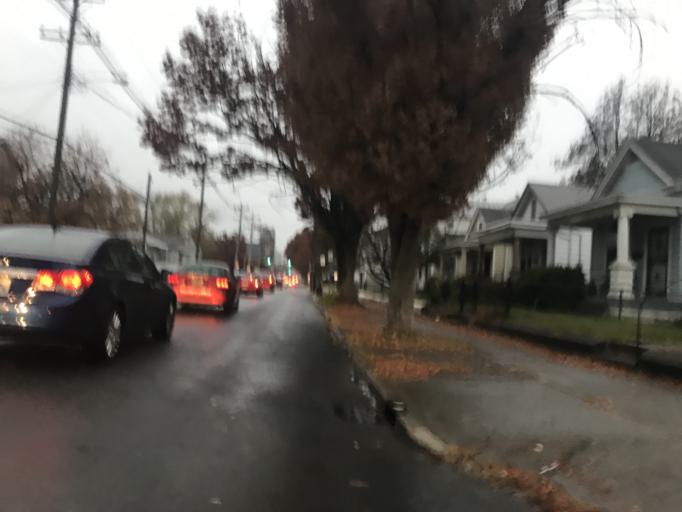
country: US
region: Kentucky
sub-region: Jefferson County
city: Louisville
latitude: 38.2358
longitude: -85.7411
